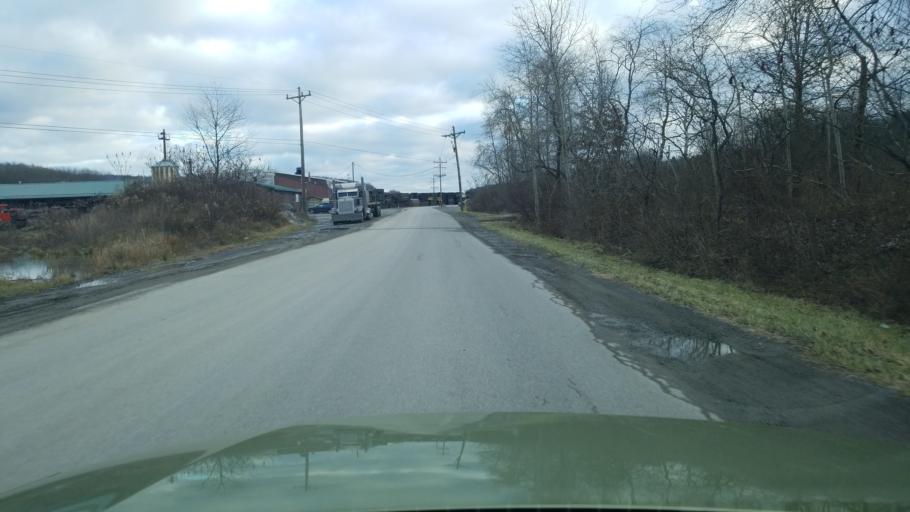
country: US
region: Pennsylvania
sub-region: Jefferson County
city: Falls Creek
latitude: 41.1410
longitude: -78.7923
